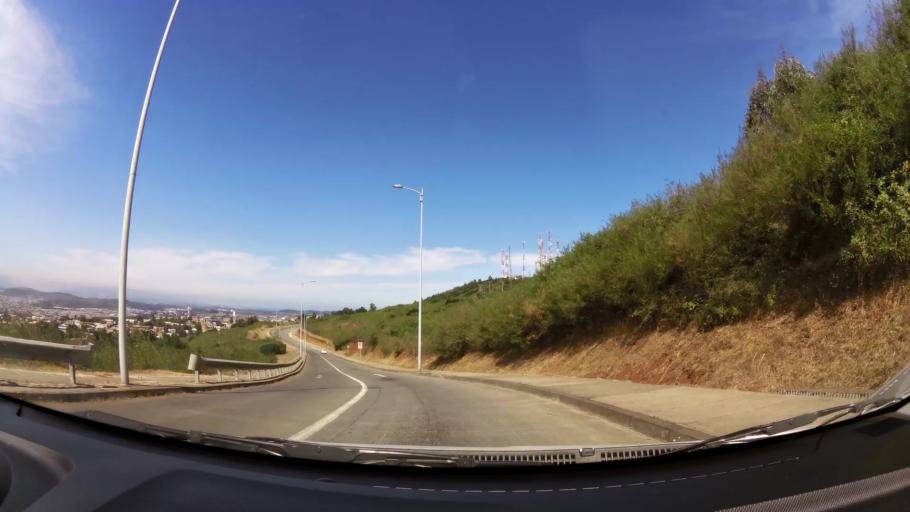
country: CL
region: Biobio
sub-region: Provincia de Concepcion
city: Talcahuano
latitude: -36.7082
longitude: -73.1232
